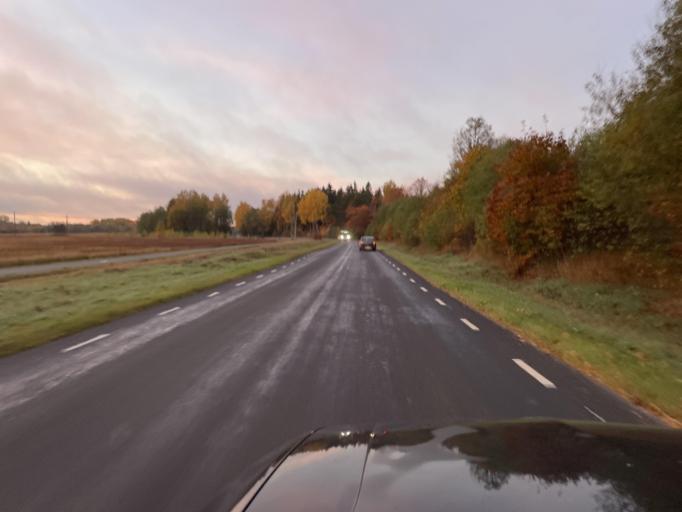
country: EE
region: Harju
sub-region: Nissi vald
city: Riisipere
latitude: 59.2392
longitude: 24.2443
